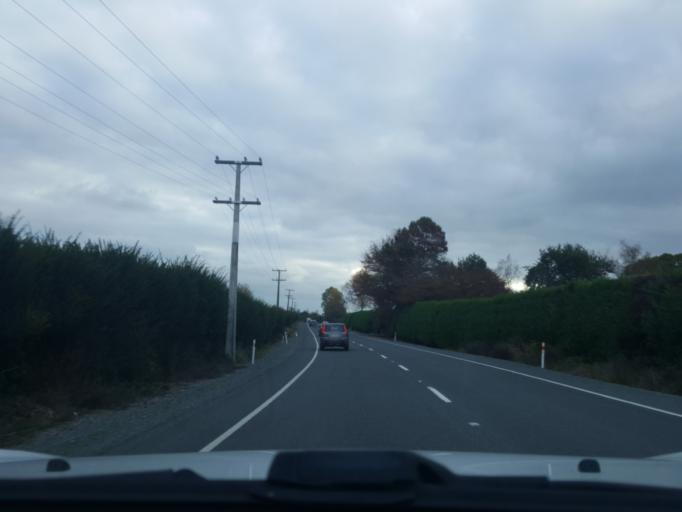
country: NZ
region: Waikato
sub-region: Matamata-Piako District
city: Matamata
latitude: -37.8663
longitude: 175.8623
